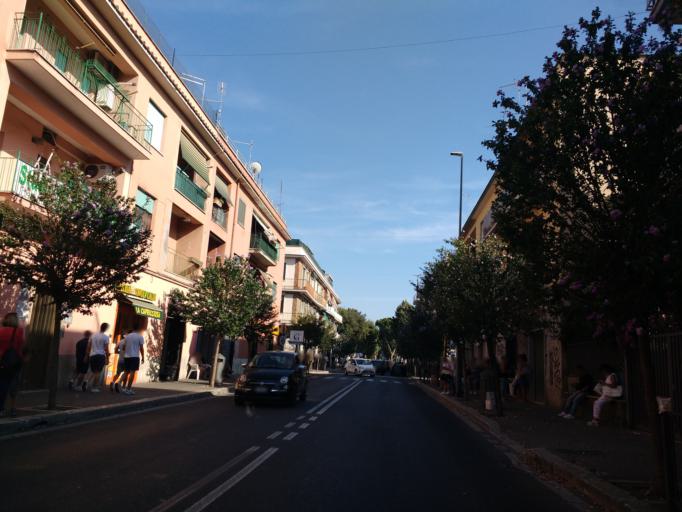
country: IT
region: Latium
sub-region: Citta metropolitana di Roma Capitale
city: Acilia-Castel Fusano-Ostia Antica
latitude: 41.7840
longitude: 12.3648
